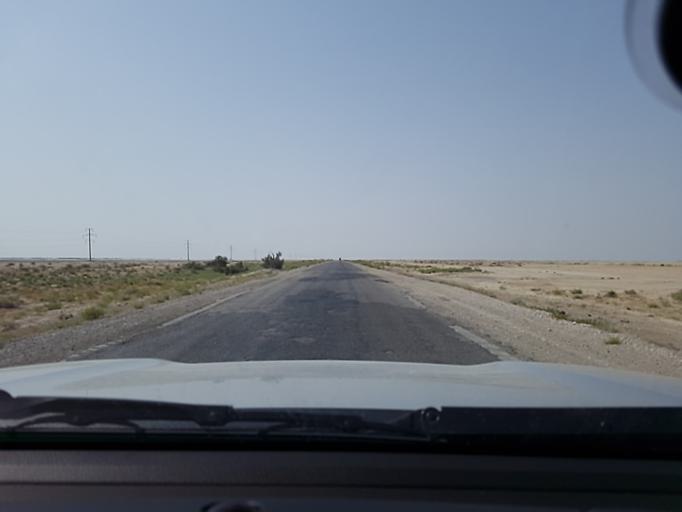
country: TM
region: Balkan
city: Gumdag
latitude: 38.8815
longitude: 54.5935
